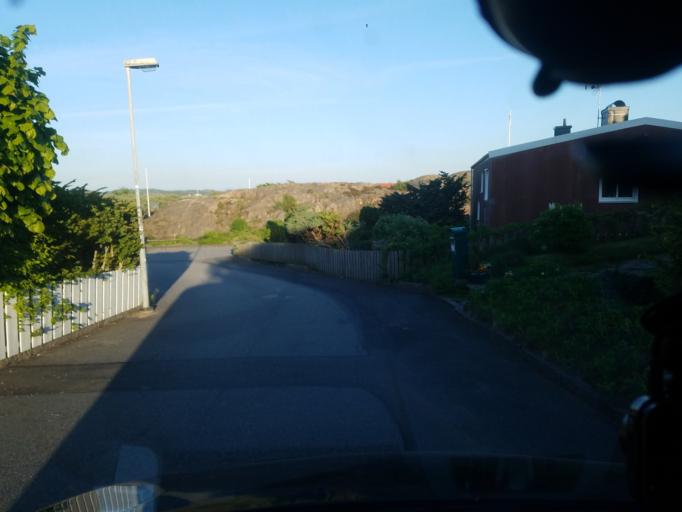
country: SE
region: Vaestra Goetaland
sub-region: Lysekils Kommun
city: Lysekil
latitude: 58.2692
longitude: 11.4273
